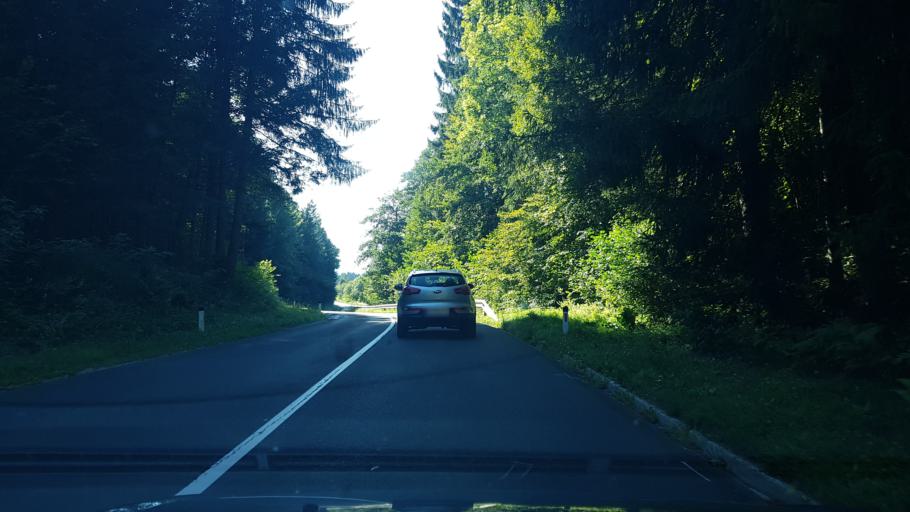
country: SI
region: Ravne na Koroskem
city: Kotlje
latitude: 46.5158
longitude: 15.0108
